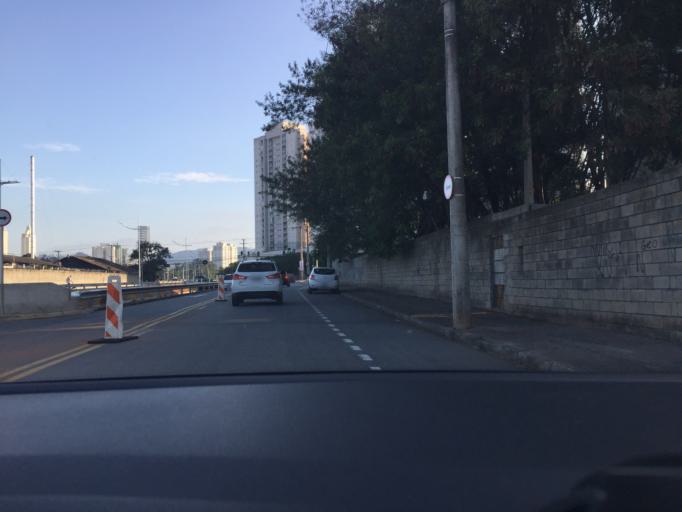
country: BR
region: Sao Paulo
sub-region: Jundiai
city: Jundiai
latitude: -23.1785
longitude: -46.9056
